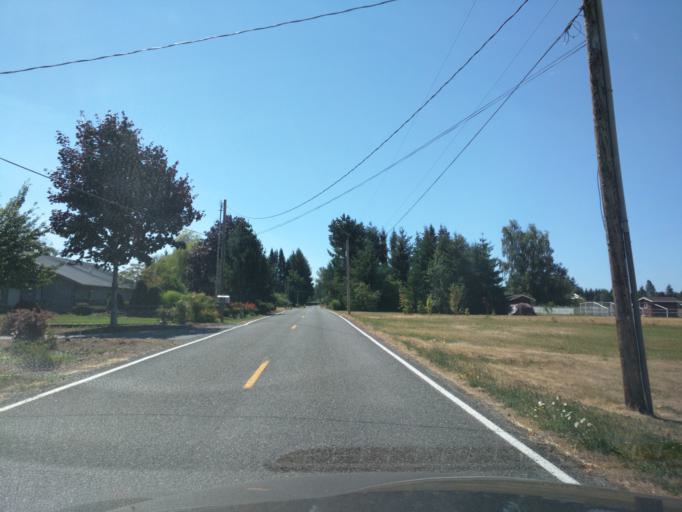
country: US
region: Washington
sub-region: Whatcom County
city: Lynden
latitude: 48.8820
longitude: -122.4147
